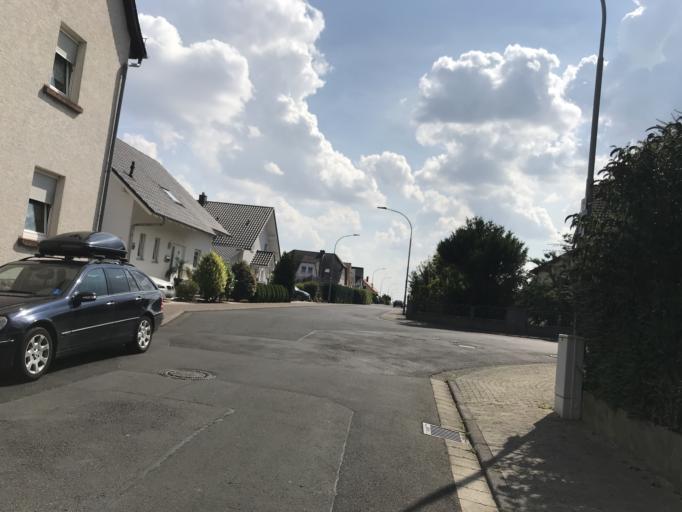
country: DE
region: Hesse
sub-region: Regierungsbezirk Darmstadt
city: Wolfersheim
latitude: 50.3925
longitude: 8.8030
